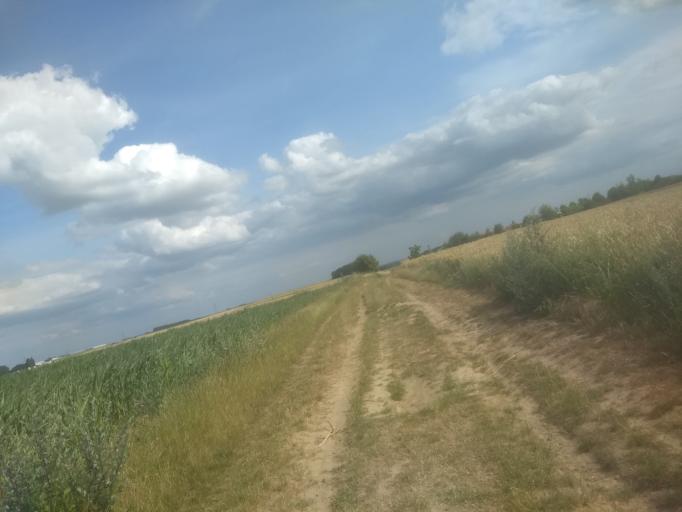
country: FR
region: Nord-Pas-de-Calais
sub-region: Departement du Pas-de-Calais
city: Beaurains
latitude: 50.2739
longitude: 2.7970
